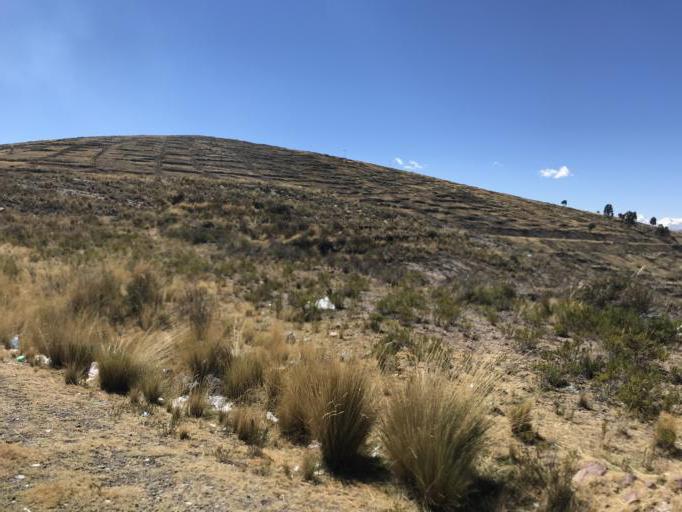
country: BO
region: La Paz
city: San Pablo
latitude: -16.2123
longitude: -68.8405
